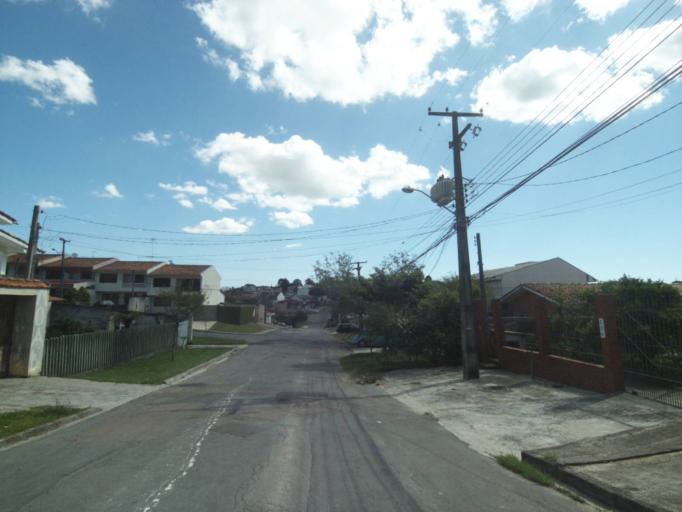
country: BR
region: Parana
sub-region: Curitiba
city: Curitiba
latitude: -25.3747
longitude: -49.2479
